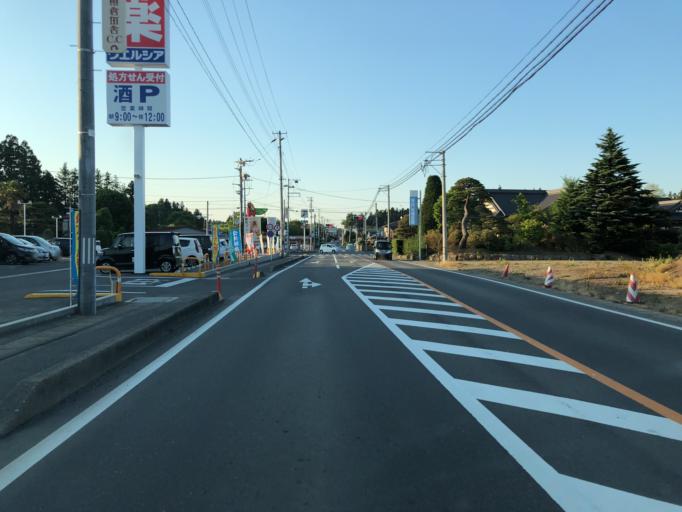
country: JP
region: Fukushima
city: Ishikawa
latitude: 37.1438
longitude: 140.3491
